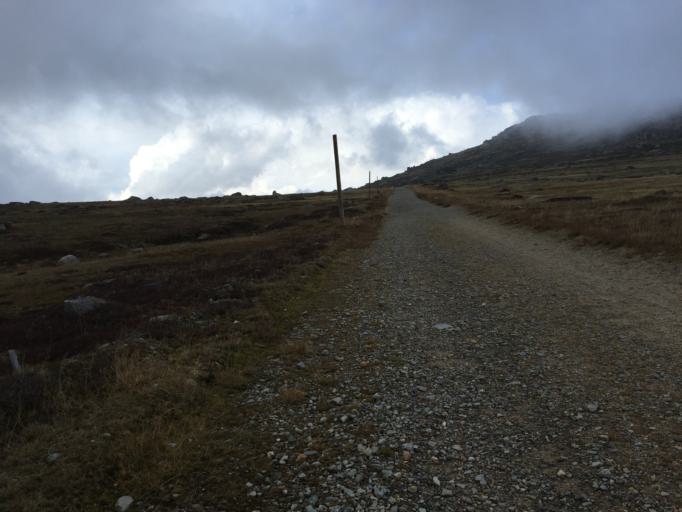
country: AU
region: New South Wales
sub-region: Snowy River
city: Jindabyne
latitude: -36.4582
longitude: 148.2975
